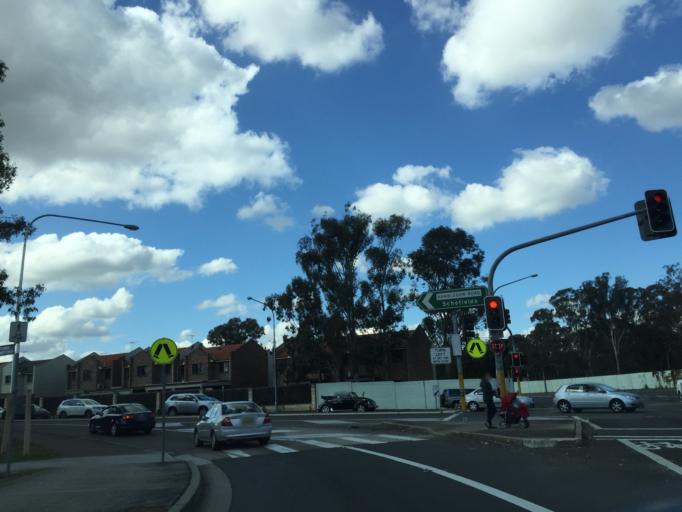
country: AU
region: New South Wales
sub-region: Blacktown
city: Quakers Hill
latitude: -33.7240
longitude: 150.8888
